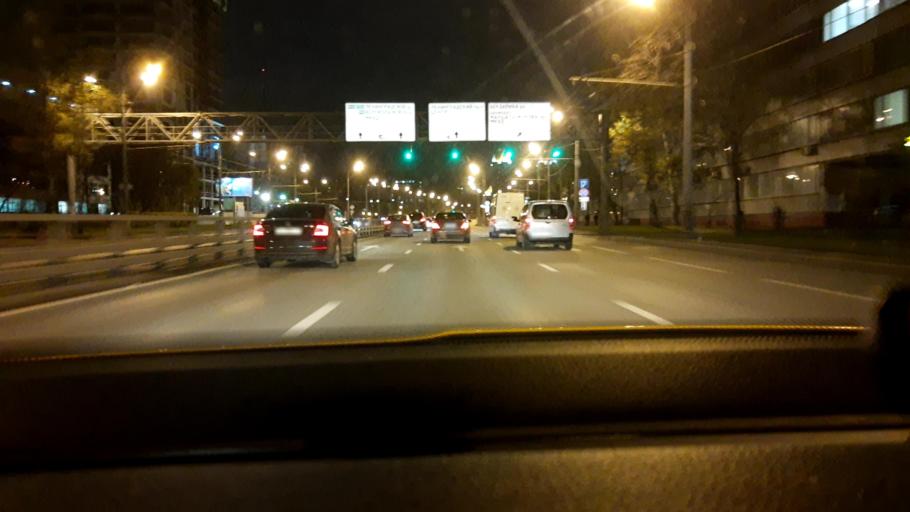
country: RU
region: Moskovskaya
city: Khoroshevo-Mnevniki
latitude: 55.7839
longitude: 37.4832
